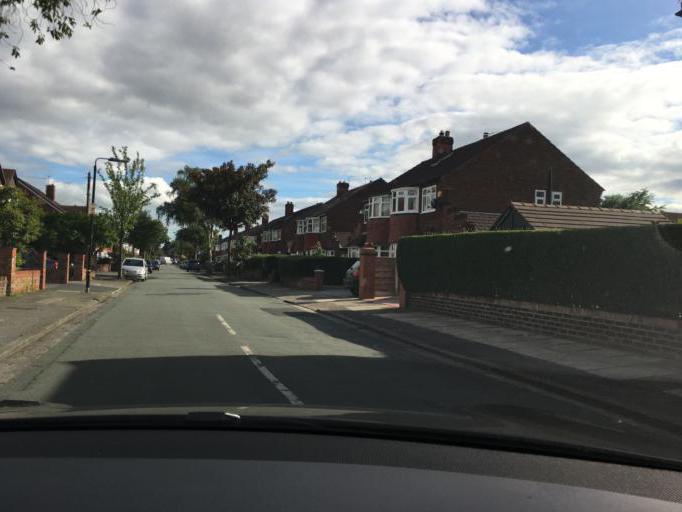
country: GB
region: England
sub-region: Trafford
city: Urmston
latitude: 53.4548
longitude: -2.3481
